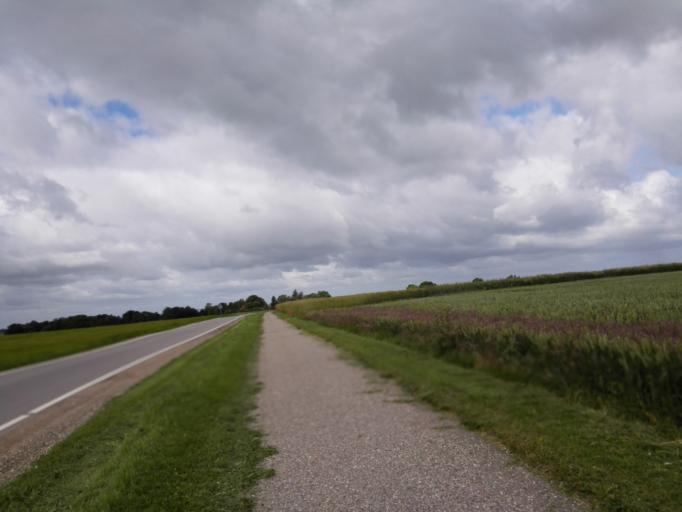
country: DK
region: Capital Region
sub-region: Egedal Kommune
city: Olstykke
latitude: 55.8068
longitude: 12.1504
